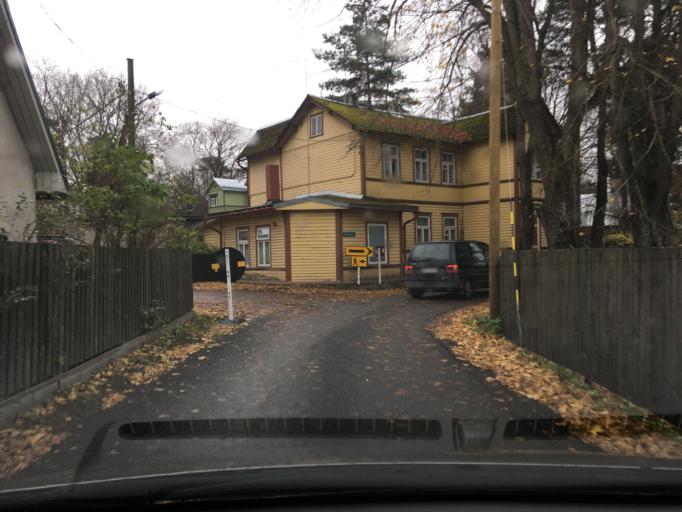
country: EE
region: Harju
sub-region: Tallinna linn
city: Tallinn
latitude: 59.3862
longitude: 24.6920
